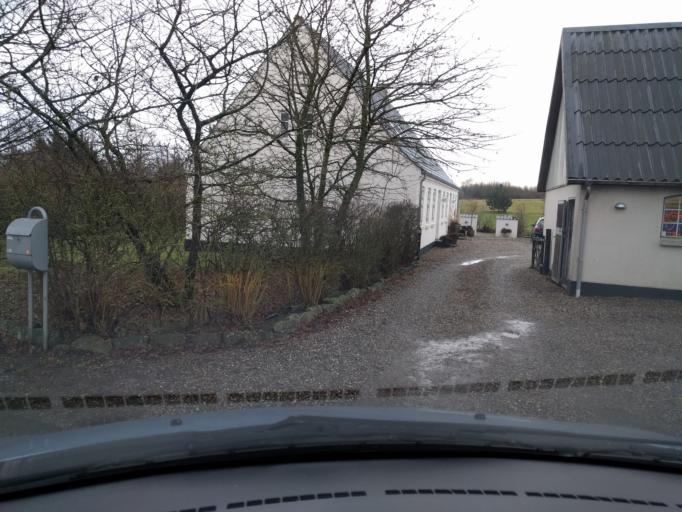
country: DK
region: South Denmark
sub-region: Kerteminde Kommune
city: Langeskov
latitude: 55.3384
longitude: 10.5408
